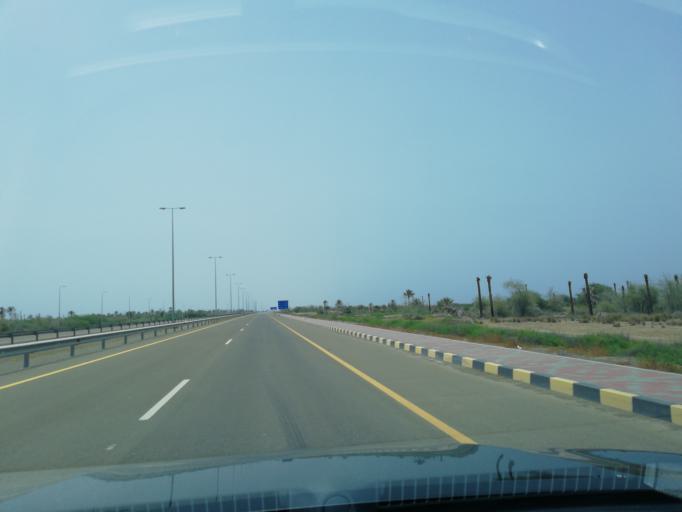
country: OM
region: Al Batinah
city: Al Liwa'
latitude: 24.6335
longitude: 56.5258
